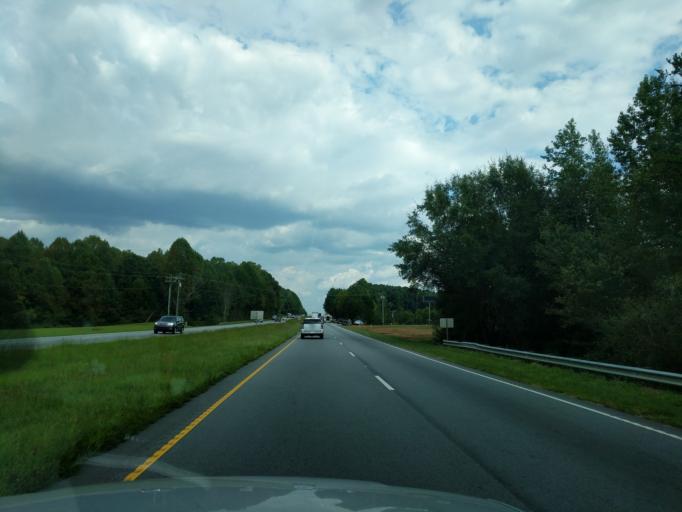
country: US
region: South Carolina
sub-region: Anderson County
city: Powdersville
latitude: 34.7940
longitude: -82.5009
